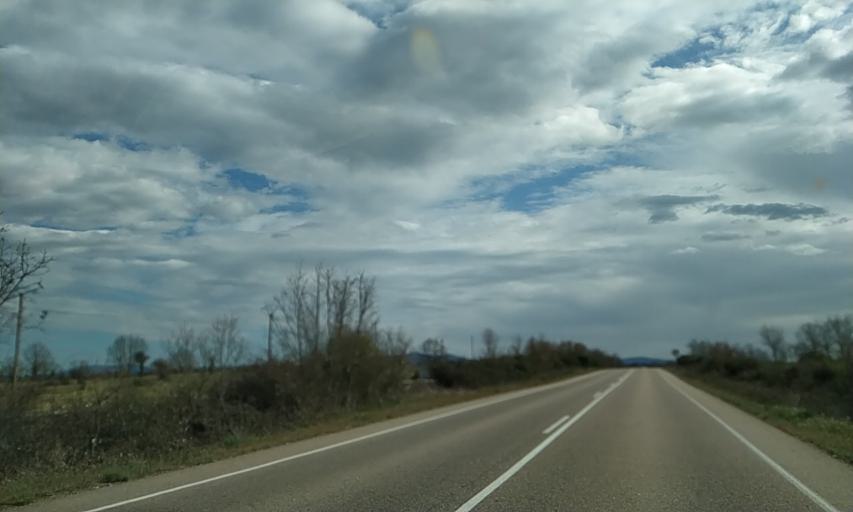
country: ES
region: Castille and Leon
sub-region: Provincia de Salamanca
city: Robleda
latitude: 40.4195
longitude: -6.6008
